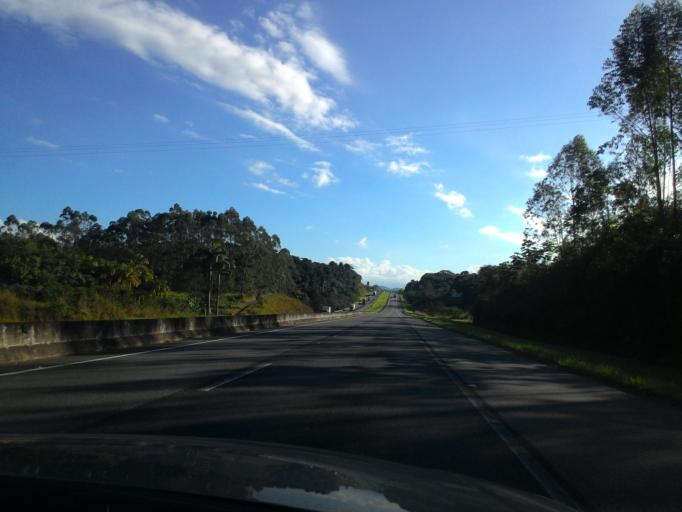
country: BR
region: Sao Paulo
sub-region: Pariquera-Acu
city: Pariquera Acu
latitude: -24.6491
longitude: -47.9312
